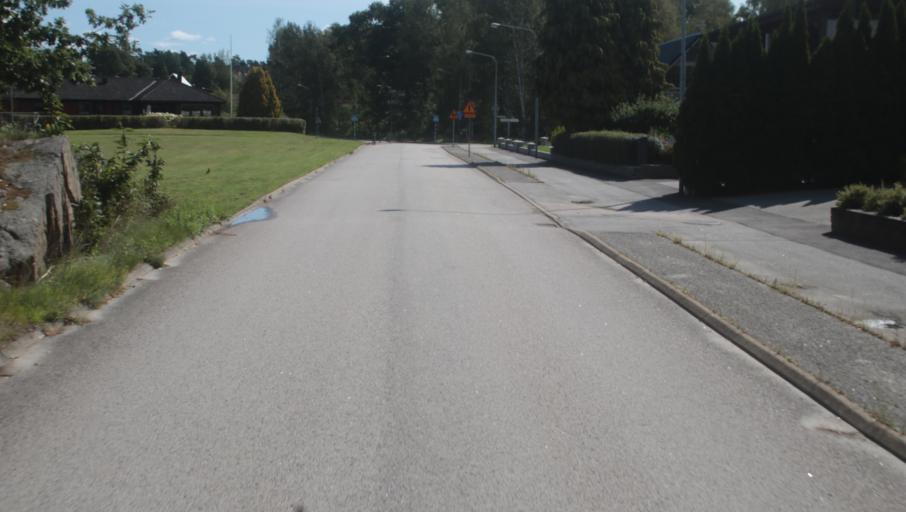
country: SE
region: Blekinge
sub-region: Karlshamns Kommun
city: Karlshamn
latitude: 56.1881
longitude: 14.8684
